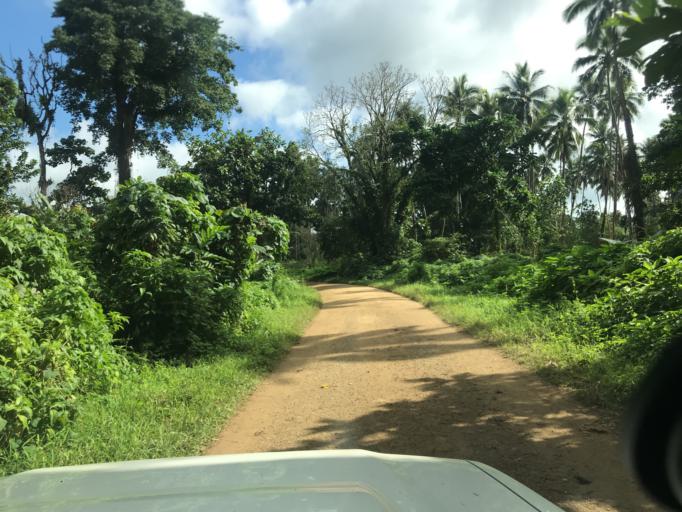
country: VU
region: Sanma
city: Luganville
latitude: -15.4754
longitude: 167.0855
